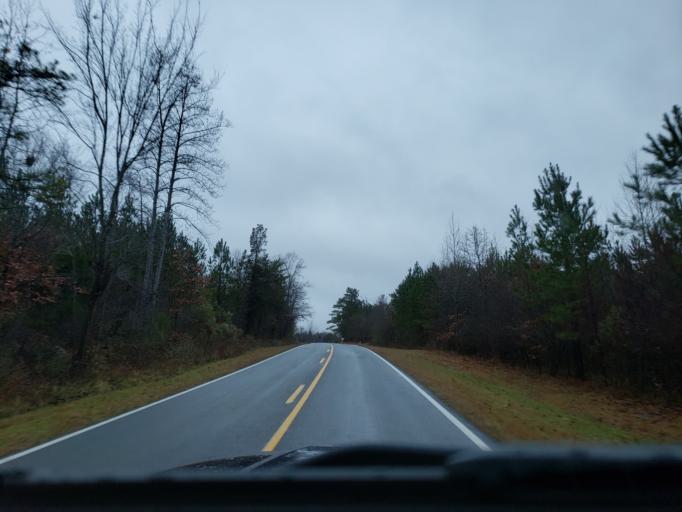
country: US
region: North Carolina
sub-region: Cleveland County
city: White Plains
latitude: 35.1934
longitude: -81.3844
